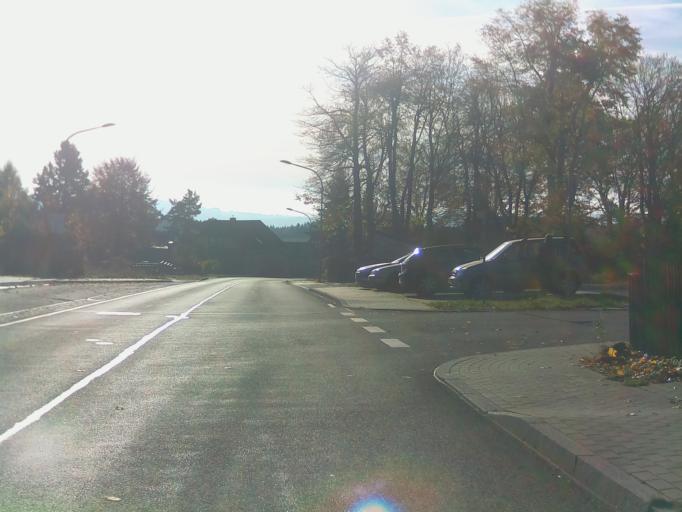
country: DE
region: Thuringia
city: Reichmannsdorf
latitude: 50.5537
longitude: 11.2600
